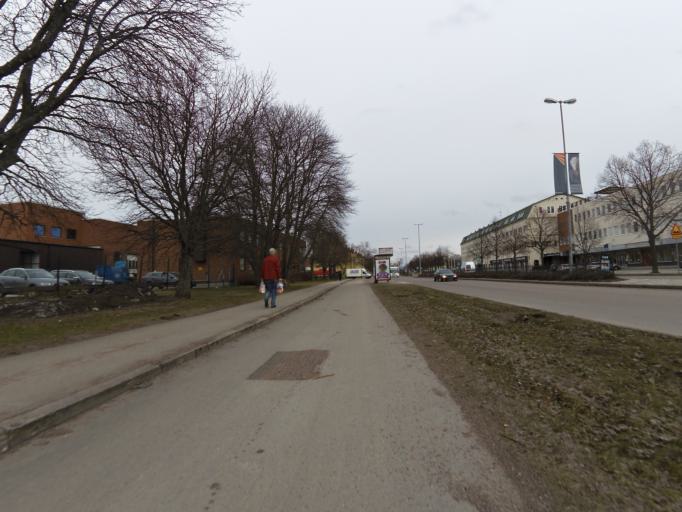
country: SE
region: Gaevleborg
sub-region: Gavle Kommun
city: Gavle
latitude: 60.6628
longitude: 17.1560
